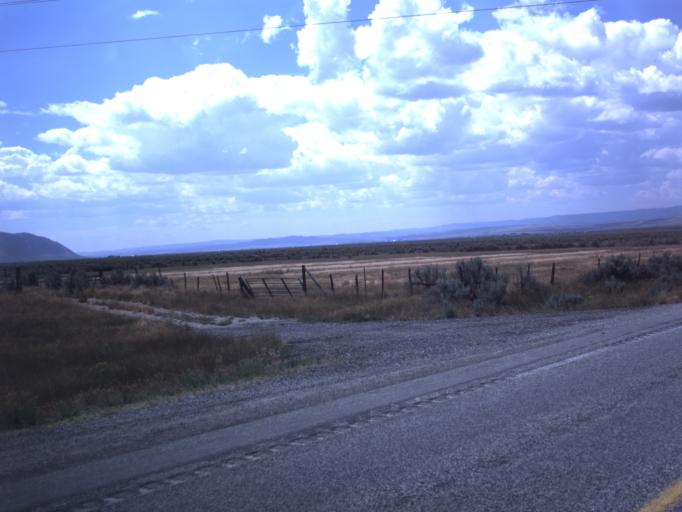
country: US
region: Utah
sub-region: Rich County
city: Randolph
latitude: 41.7798
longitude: -111.0460
